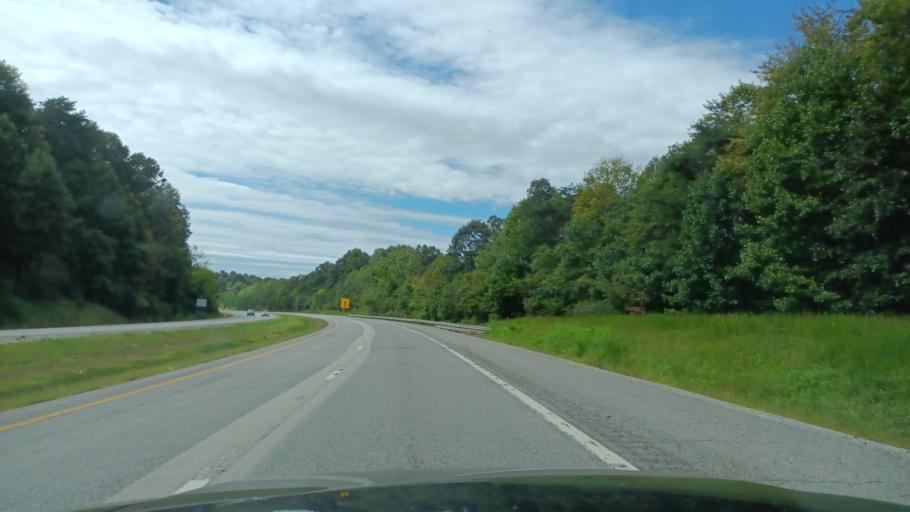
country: US
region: West Virginia
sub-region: Ritchie County
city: Pennsboro
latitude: 39.2754
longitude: -80.8797
